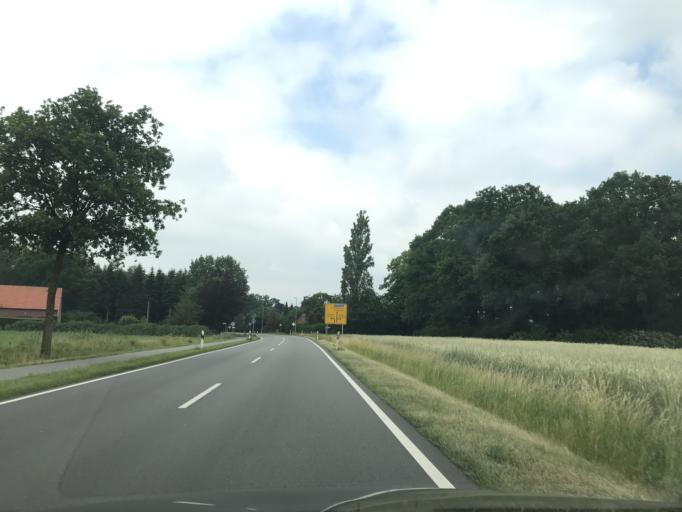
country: DE
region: Lower Saxony
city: Kirchseelte
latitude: 52.9626
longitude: 8.7146
